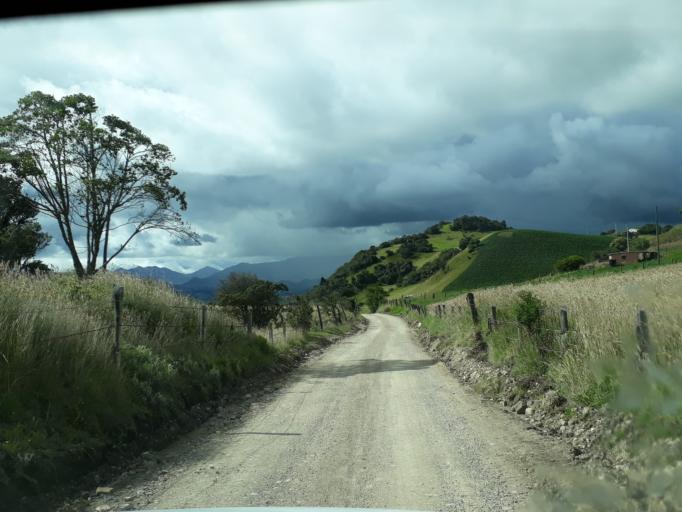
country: CO
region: Cundinamarca
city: La Mesa
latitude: 5.2619
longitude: -73.8945
